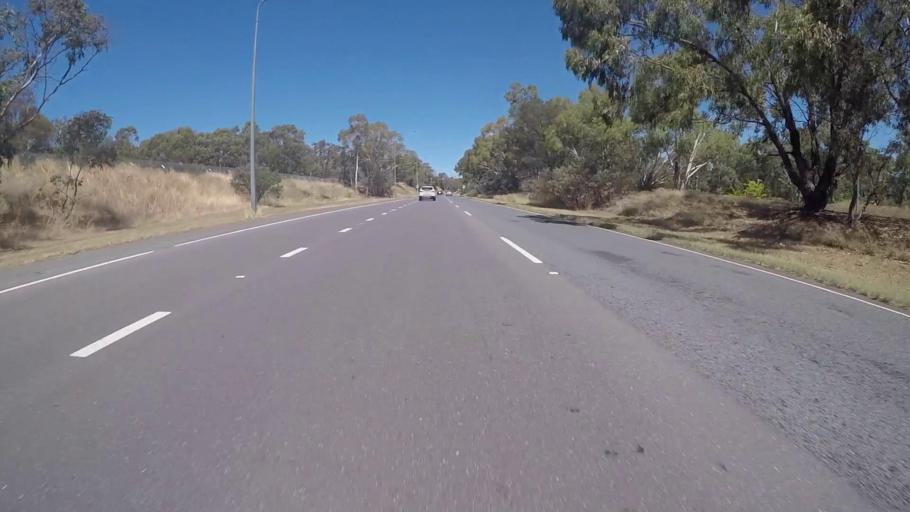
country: AU
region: Australian Capital Territory
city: Forrest
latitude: -35.3540
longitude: 149.0703
